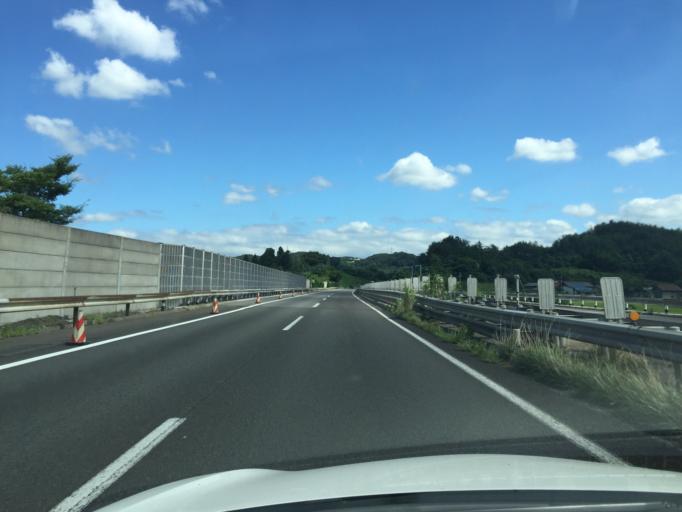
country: JP
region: Fukushima
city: Fukushima-shi
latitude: 37.7145
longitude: 140.4413
